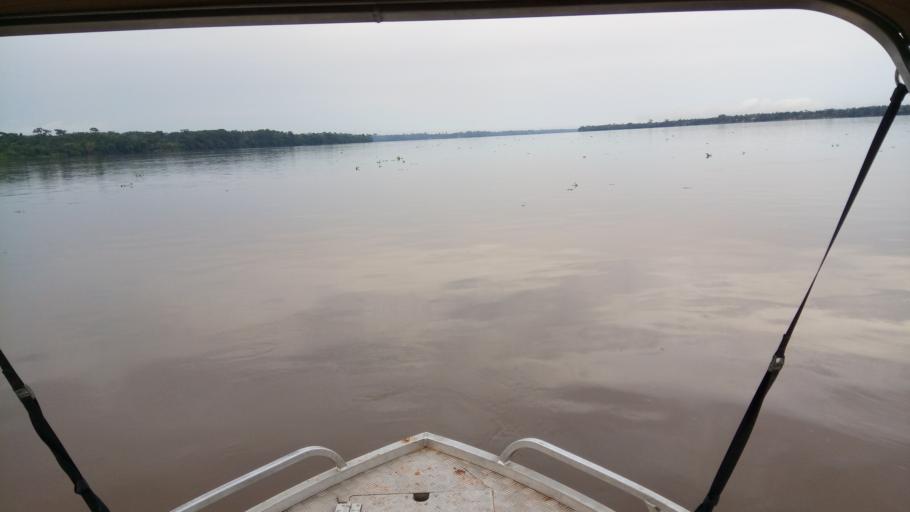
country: CD
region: Eastern Province
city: Kisangani
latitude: 0.5745
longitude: 24.8106
